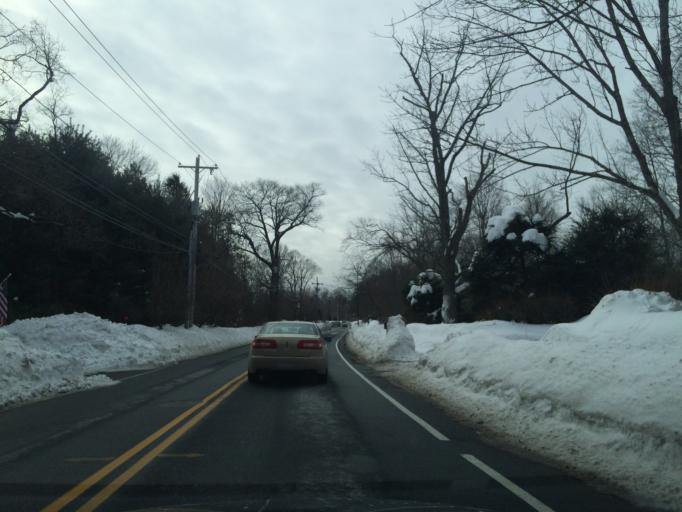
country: US
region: Massachusetts
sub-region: Middlesex County
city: Weston
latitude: 42.3450
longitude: -71.3055
